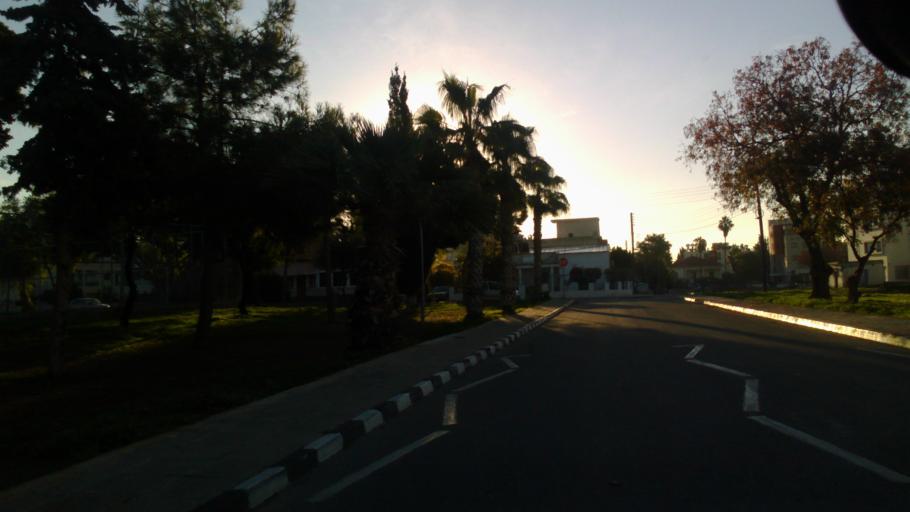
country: CY
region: Pafos
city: Paphos
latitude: 34.7787
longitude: 32.4275
